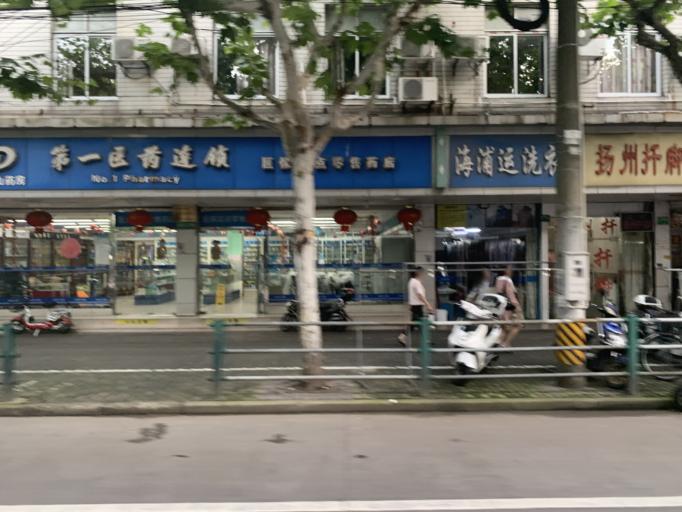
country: CN
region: Shanghai Shi
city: Huamu
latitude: 31.2436
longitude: 121.5666
